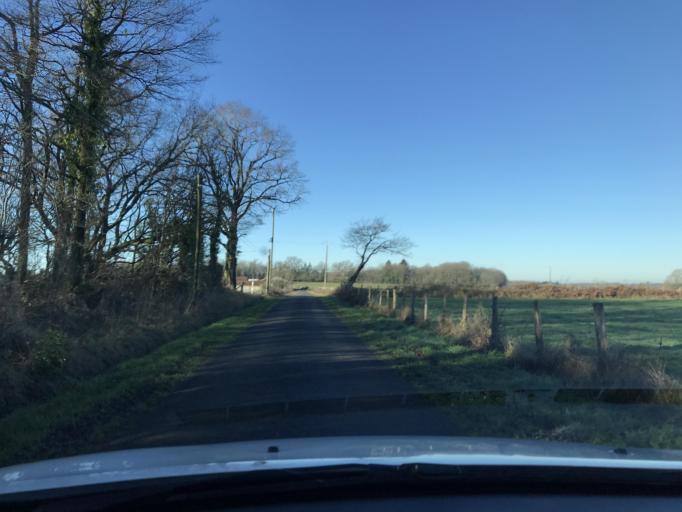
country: FR
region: Poitou-Charentes
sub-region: Departement de la Charente
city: Chasseneuil-sur-Bonnieure
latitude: 45.8392
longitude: 0.5284
